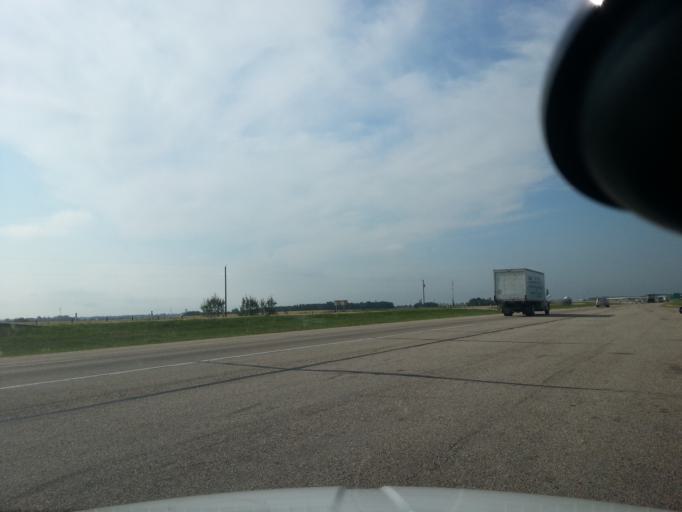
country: CA
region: Alberta
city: Red Deer
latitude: 52.3330
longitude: -113.8556
